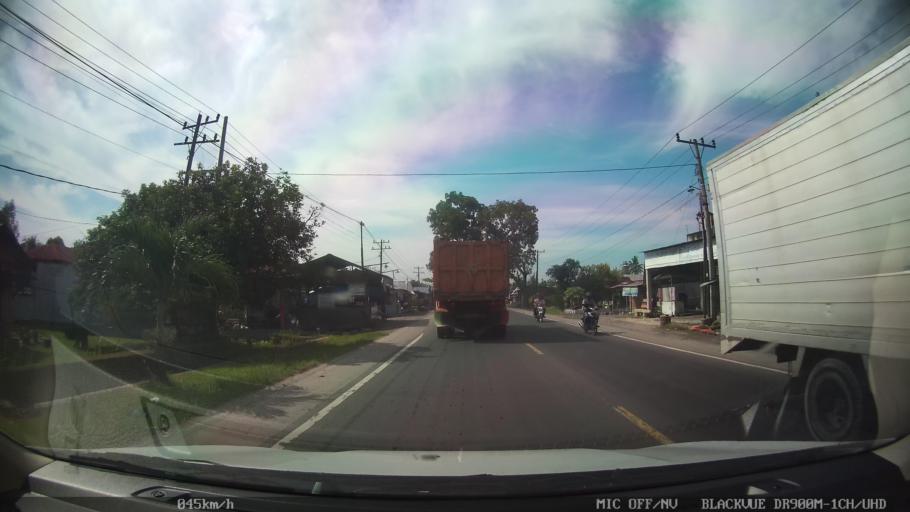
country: ID
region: North Sumatra
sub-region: Kabupaten Langkat
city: Stabat
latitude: 3.7193
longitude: 98.5032
